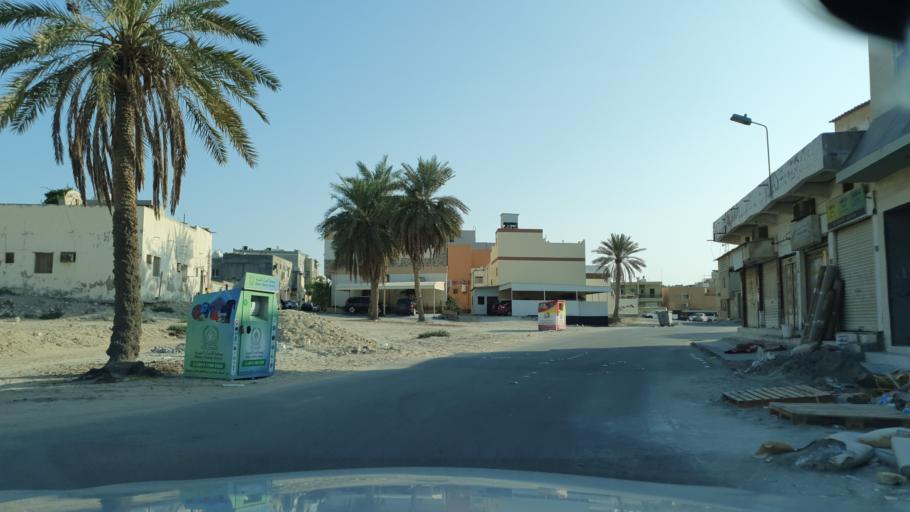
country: BH
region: Manama
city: Jidd Hafs
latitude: 26.2198
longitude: 50.4638
